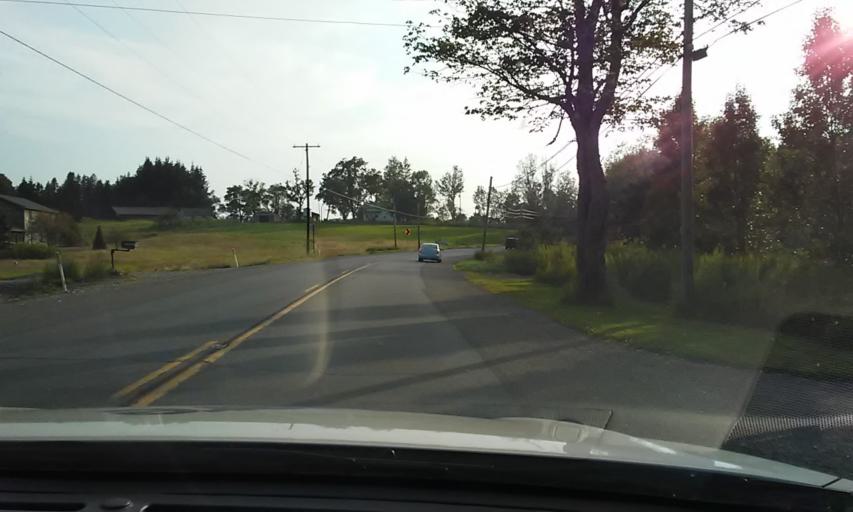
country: US
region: Pennsylvania
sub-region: McKean County
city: Kane
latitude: 41.6996
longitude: -78.7093
